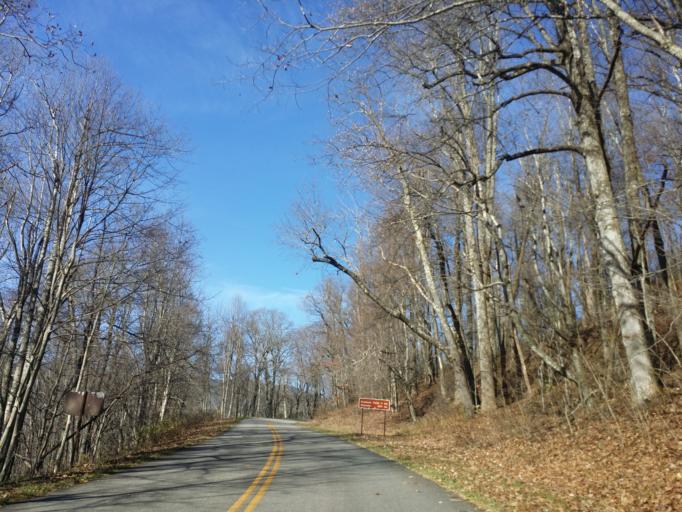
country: US
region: North Carolina
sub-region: Mitchell County
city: Spruce Pine
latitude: 35.7724
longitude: -82.1676
